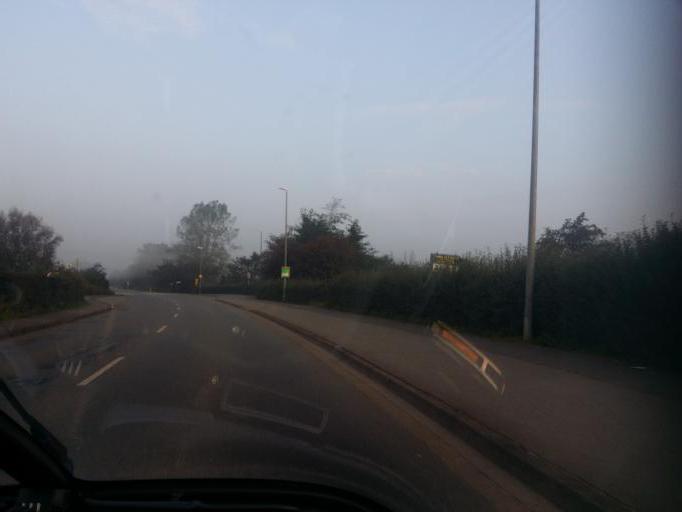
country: DE
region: Schleswig-Holstein
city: Husum
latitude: 54.4936
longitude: 9.0323
